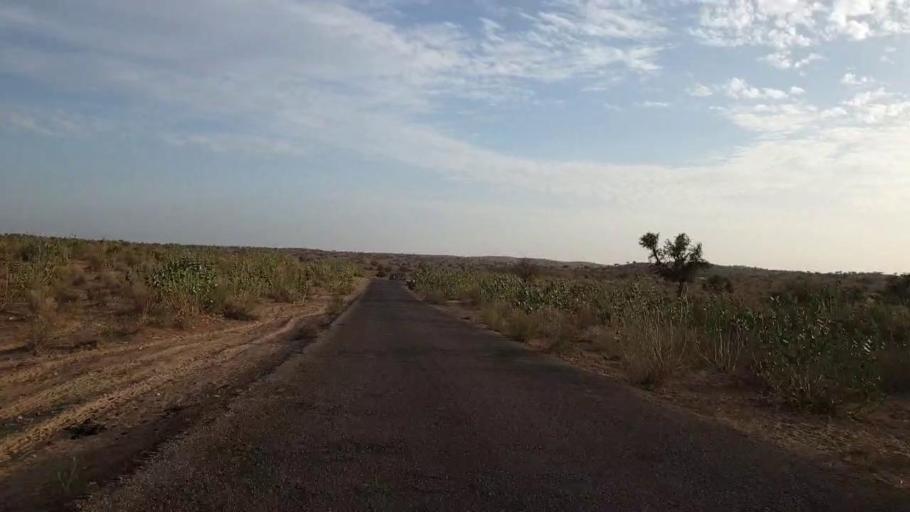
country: PK
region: Sindh
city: Umarkot
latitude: 25.1473
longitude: 70.0132
